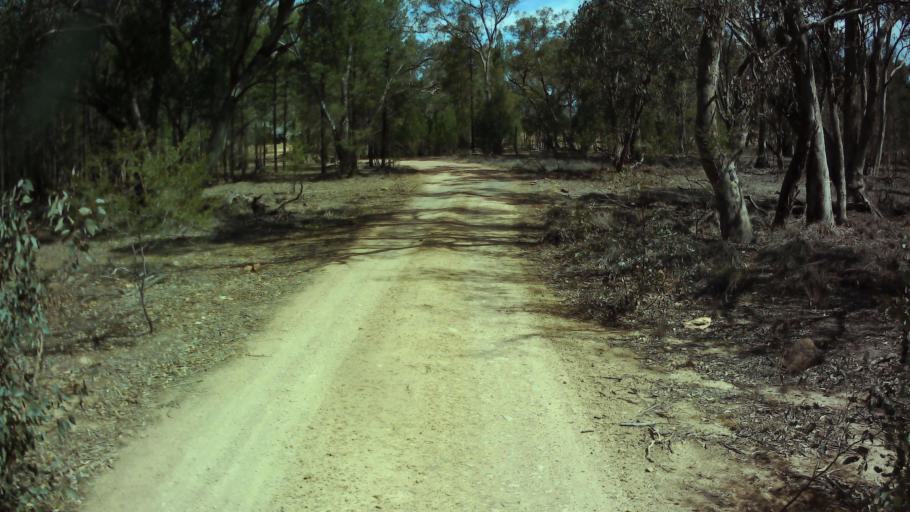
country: AU
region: New South Wales
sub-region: Weddin
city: Grenfell
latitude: -33.6744
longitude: 148.2882
